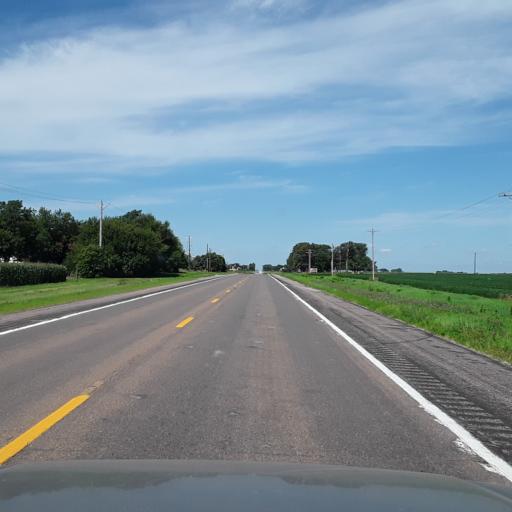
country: US
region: Nebraska
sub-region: Seward County
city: Seward
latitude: 40.9017
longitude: -97.1546
